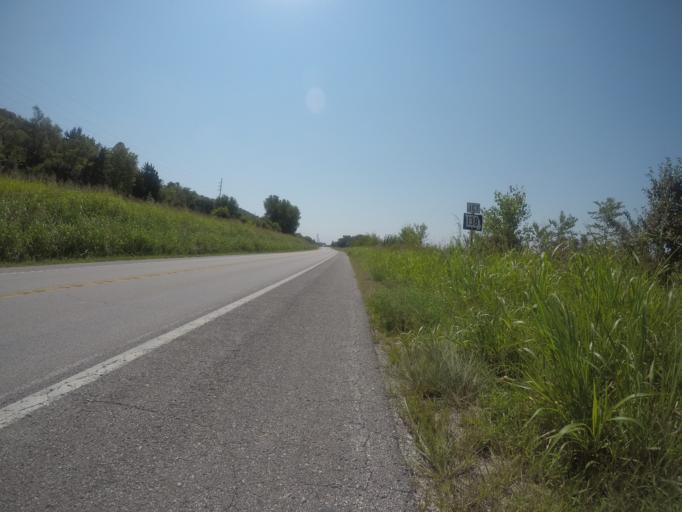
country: US
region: Kansas
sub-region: Atchison County
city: Atchison
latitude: 39.5450
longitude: -95.0441
